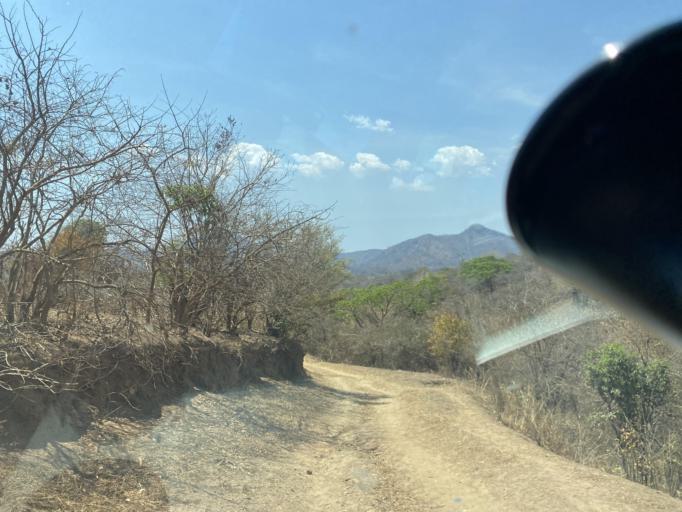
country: ZM
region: Lusaka
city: Kafue
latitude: -15.7775
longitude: 28.4586
